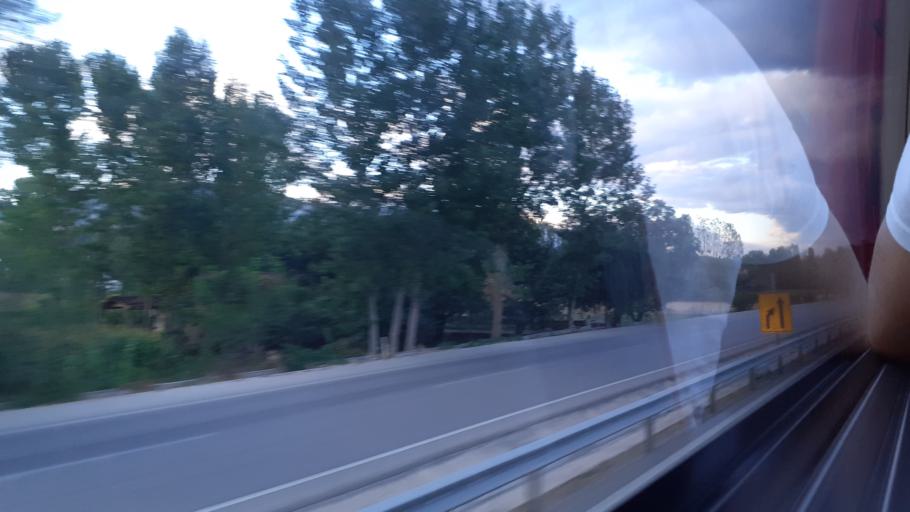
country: TR
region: Tokat
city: Dokmetepe
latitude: 40.3222
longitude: 36.2215
